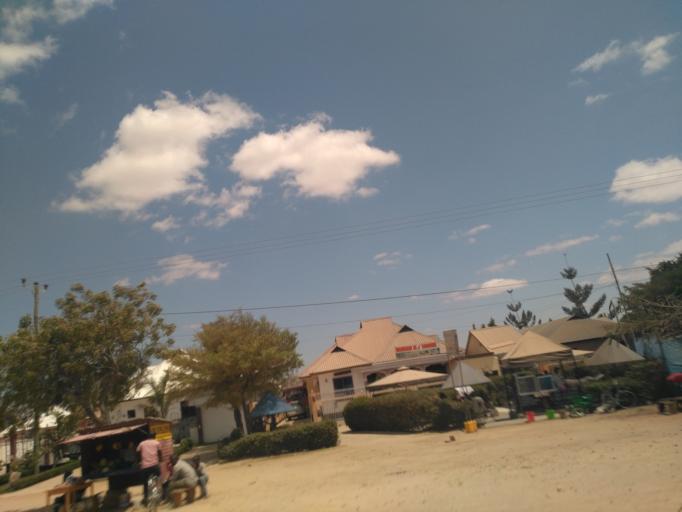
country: TZ
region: Dodoma
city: Kisasa
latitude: -6.1641
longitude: 35.7875
